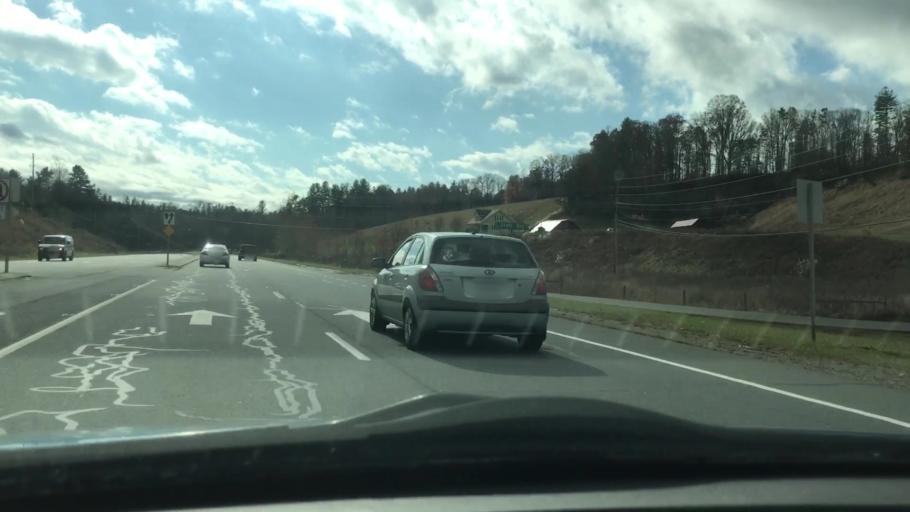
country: US
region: North Carolina
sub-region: Madison County
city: Mars Hill
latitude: 35.8621
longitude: -82.4855
